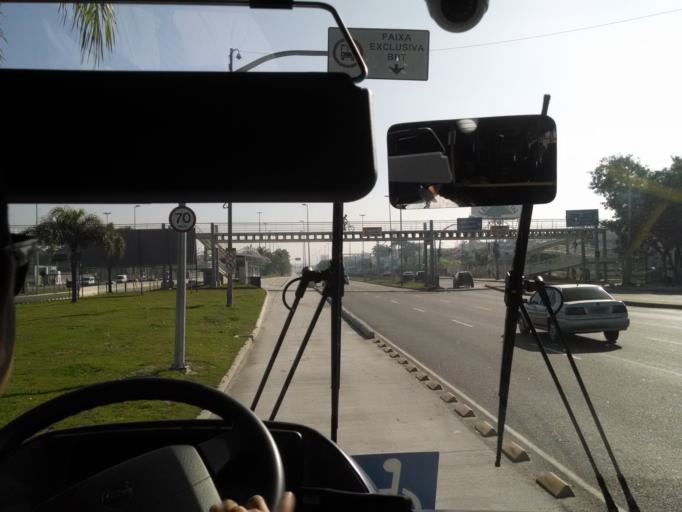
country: BR
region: Rio de Janeiro
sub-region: Rio De Janeiro
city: Rio de Janeiro
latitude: -22.9959
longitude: -43.3658
